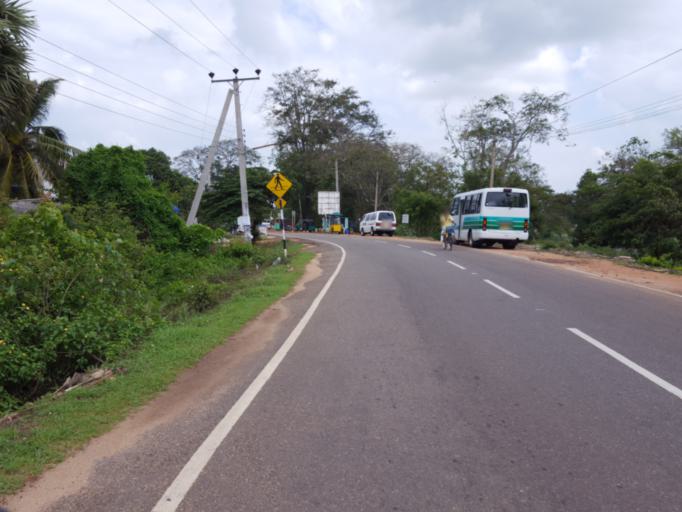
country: LK
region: North Central
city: Anuradhapura
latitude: 8.3418
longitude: 80.3811
